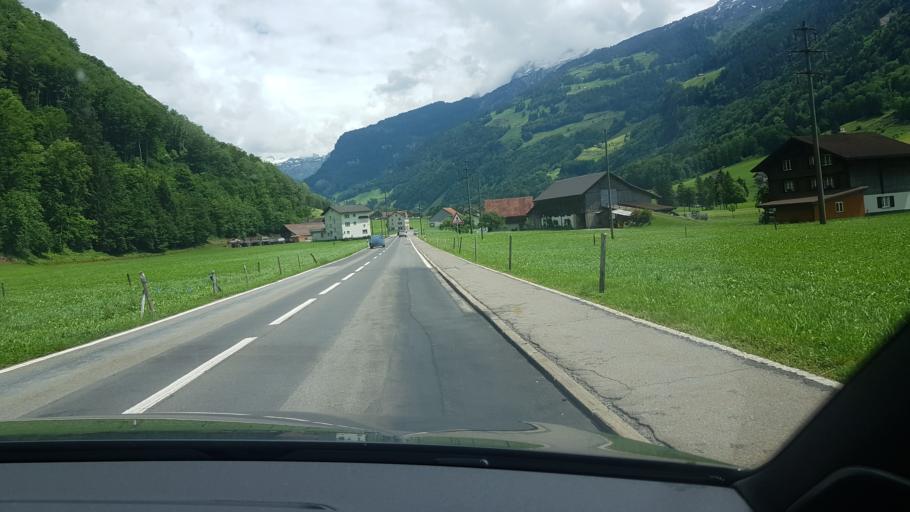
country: CH
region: Schwyz
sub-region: Bezirk Schwyz
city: Muotathal
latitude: 46.9853
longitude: 8.7207
